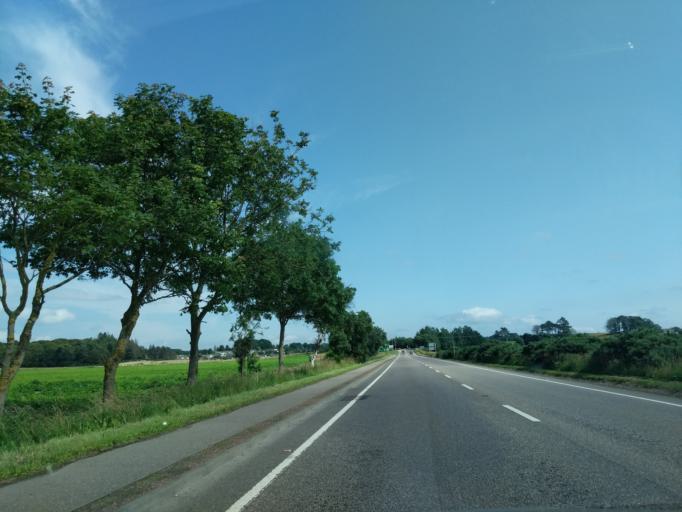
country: GB
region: Scotland
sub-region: Moray
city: Lhanbryd
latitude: 57.6368
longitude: -3.2404
